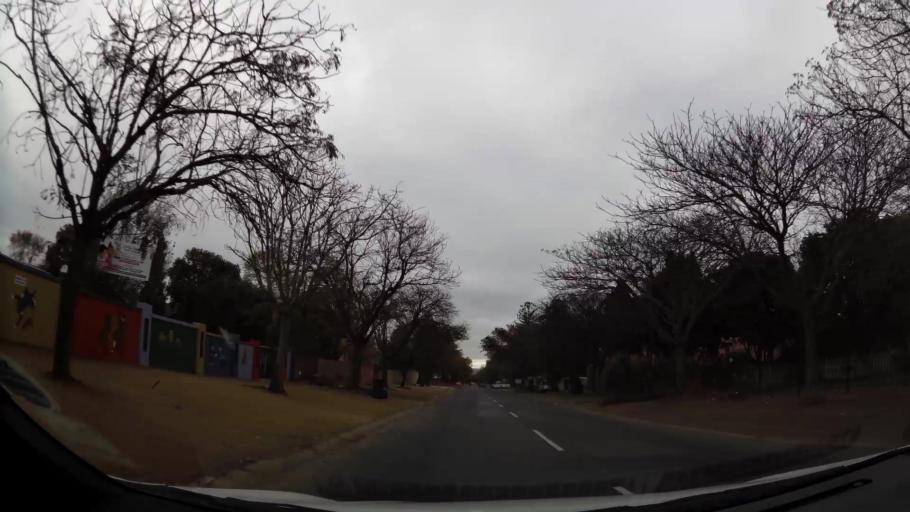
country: ZA
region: Limpopo
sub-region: Capricorn District Municipality
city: Polokwane
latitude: -23.9012
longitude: 29.4694
